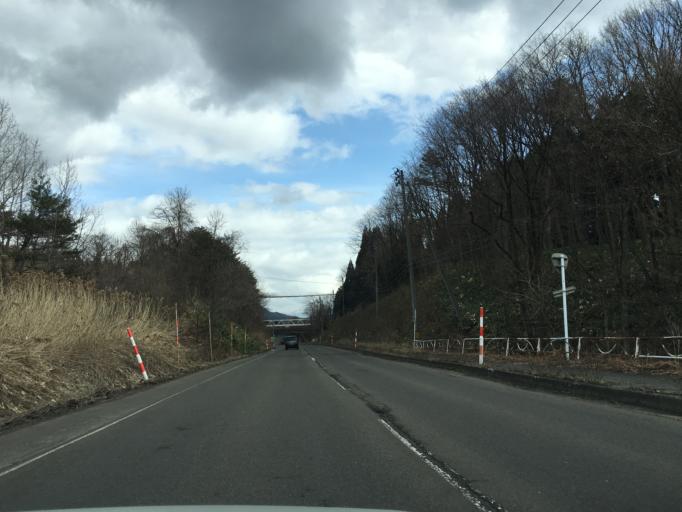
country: JP
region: Akita
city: Odate
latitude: 40.2184
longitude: 140.6414
